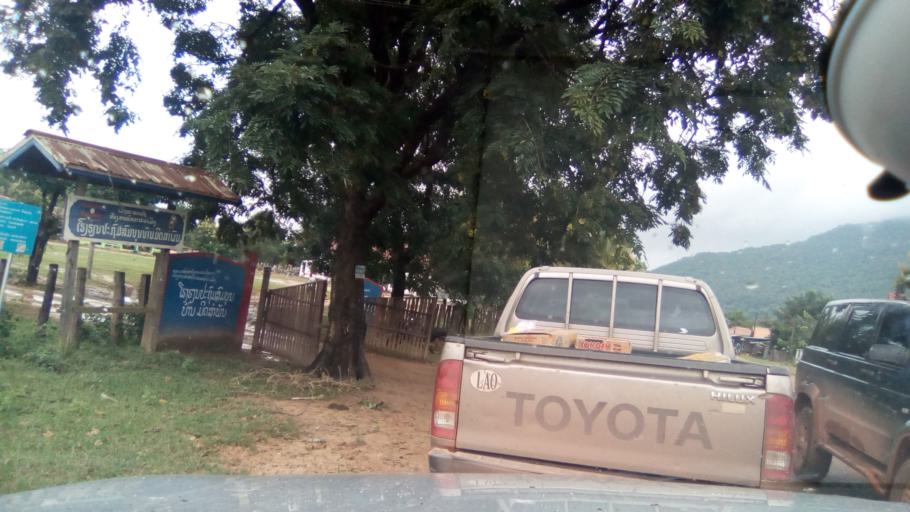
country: LA
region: Attapu
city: Attapu
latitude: 14.6826
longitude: 106.5824
